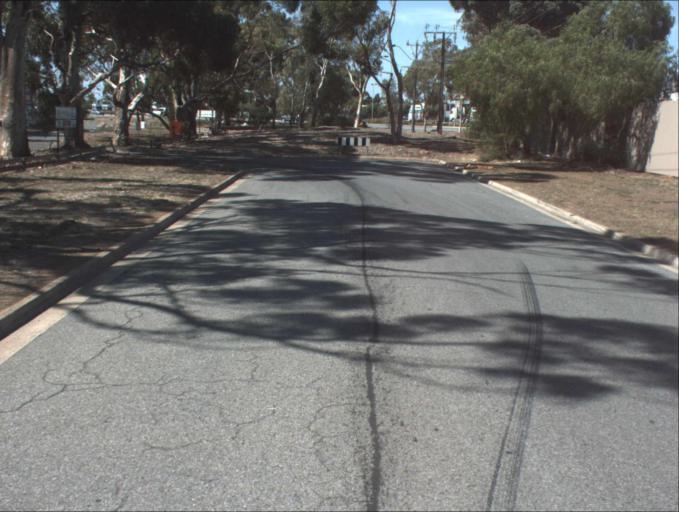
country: AU
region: South Australia
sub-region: Port Adelaide Enfield
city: Enfield
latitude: -34.8360
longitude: 138.5981
